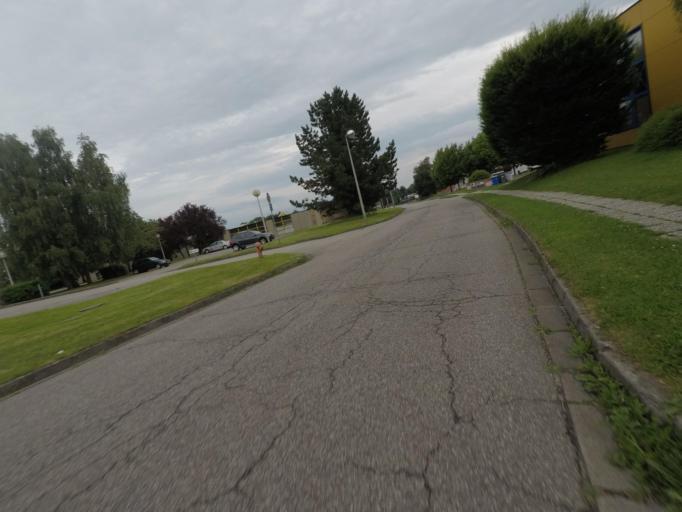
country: FR
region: Haute-Normandie
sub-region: Departement de la Seine-Maritime
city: Mont-Saint-Aignan
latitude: 49.4736
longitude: 1.0963
